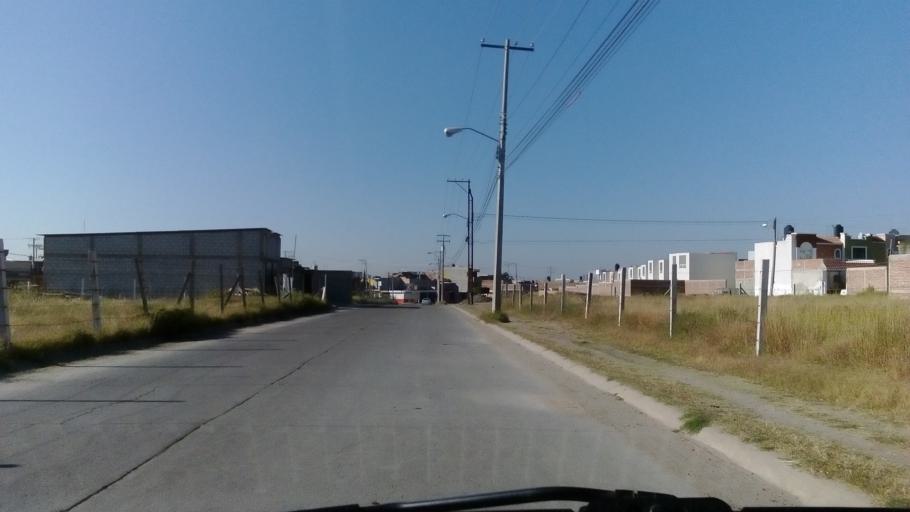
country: MX
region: Guanajuato
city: Leon
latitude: 21.1107
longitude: -101.7087
